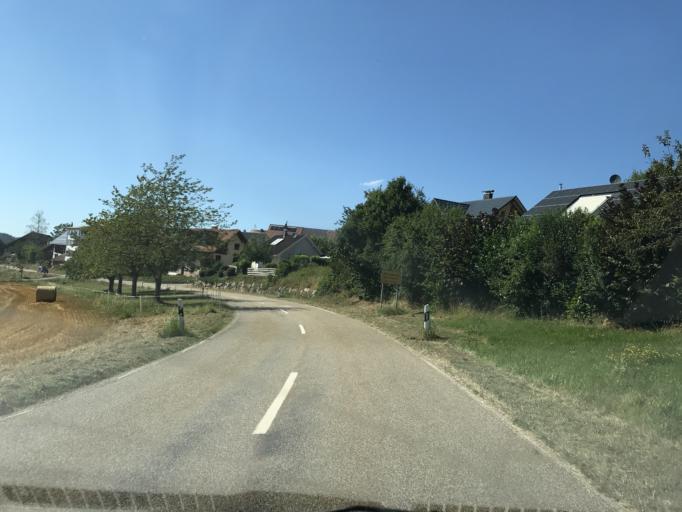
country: DE
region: Baden-Wuerttemberg
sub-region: Freiburg Region
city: Hasel
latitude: 47.6644
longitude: 7.8721
